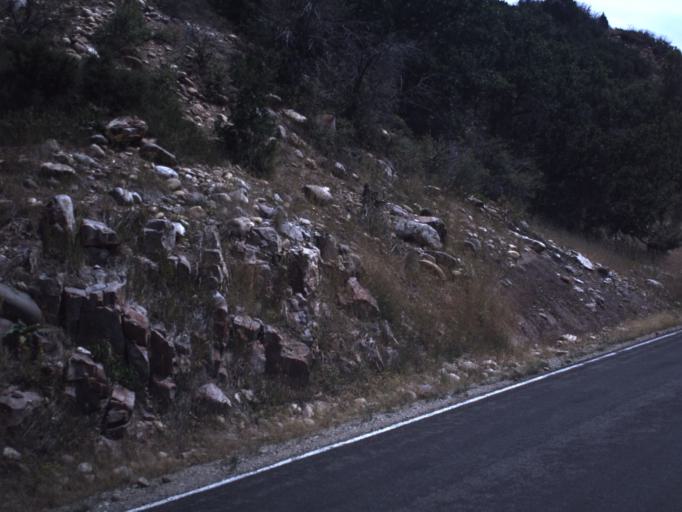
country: US
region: Utah
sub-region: Summit County
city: Francis
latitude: 40.5569
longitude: -111.1650
